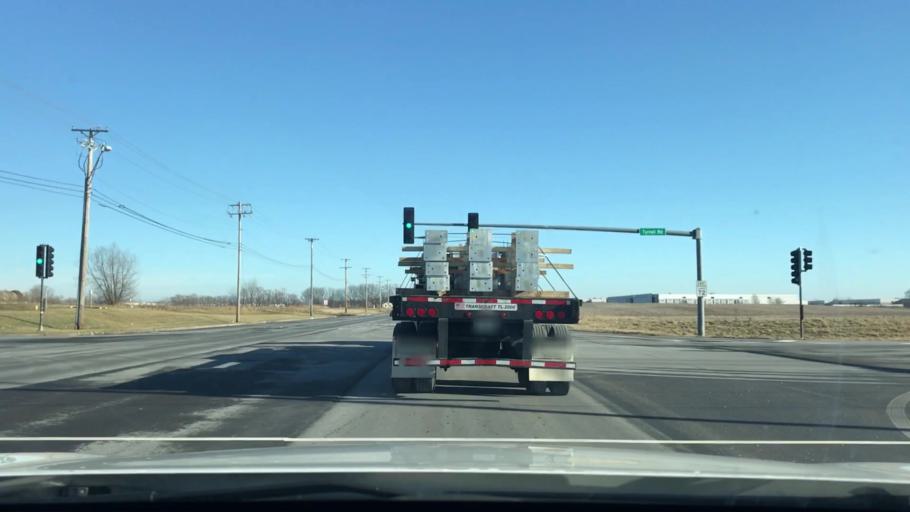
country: US
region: Illinois
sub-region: Kane County
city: Gilberts
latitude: 42.1033
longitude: -88.3599
